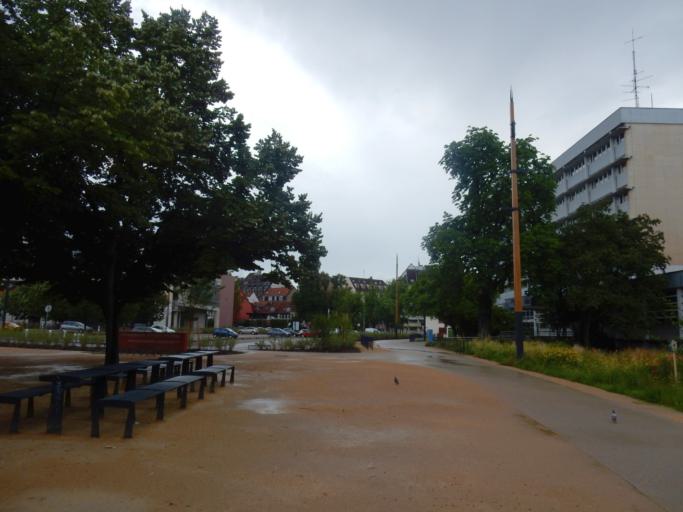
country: FR
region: Alsace
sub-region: Departement du Bas-Rhin
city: Strasbourg
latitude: 48.5793
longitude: 7.7636
